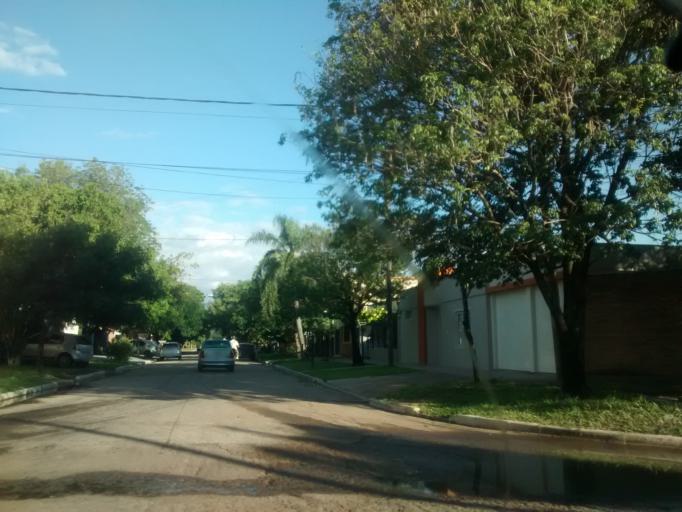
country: AR
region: Chaco
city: Resistencia
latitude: -27.4648
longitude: -58.9948
